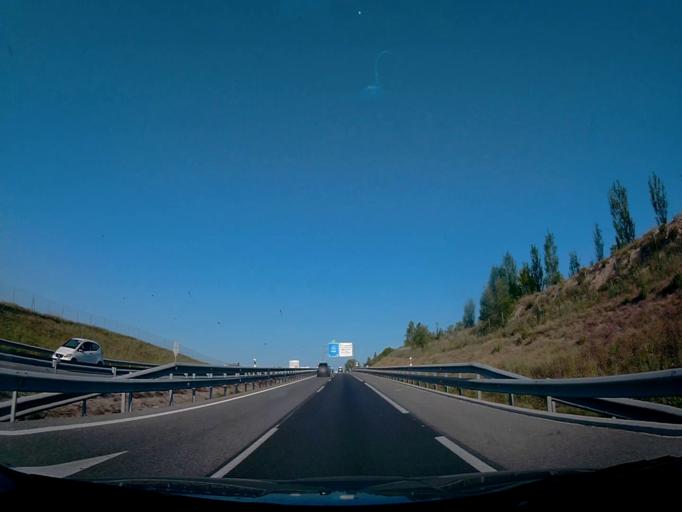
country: ES
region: Madrid
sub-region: Provincia de Madrid
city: Navalcarnero
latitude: 40.2796
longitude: -4.0193
